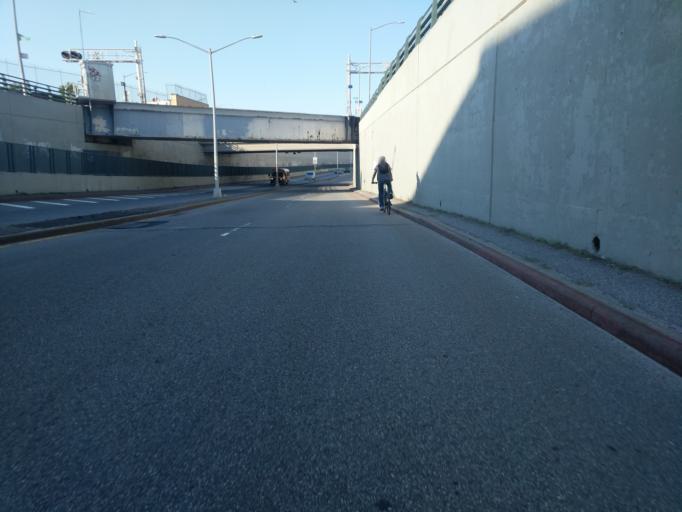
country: US
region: New York
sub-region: Queens County
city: Long Island City
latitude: 40.7160
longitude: -73.9118
